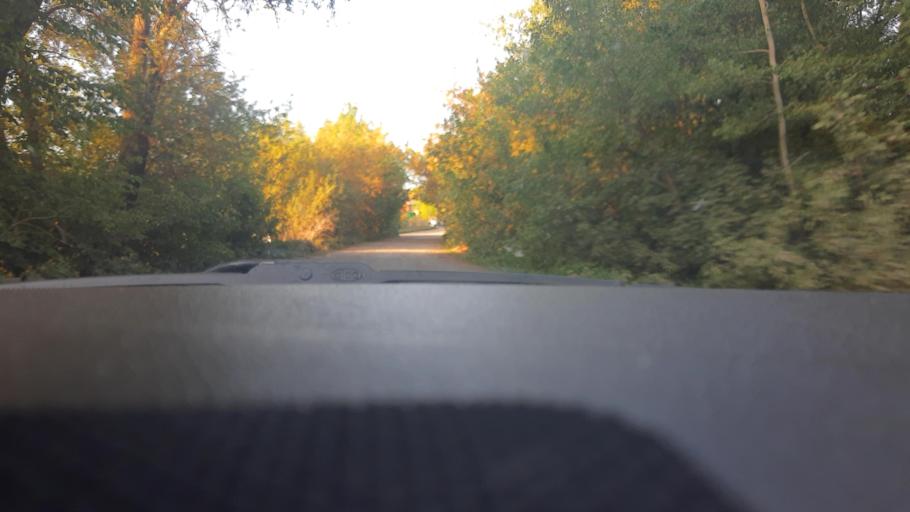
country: RU
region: Bashkortostan
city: Avdon
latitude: 54.6398
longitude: 55.5511
